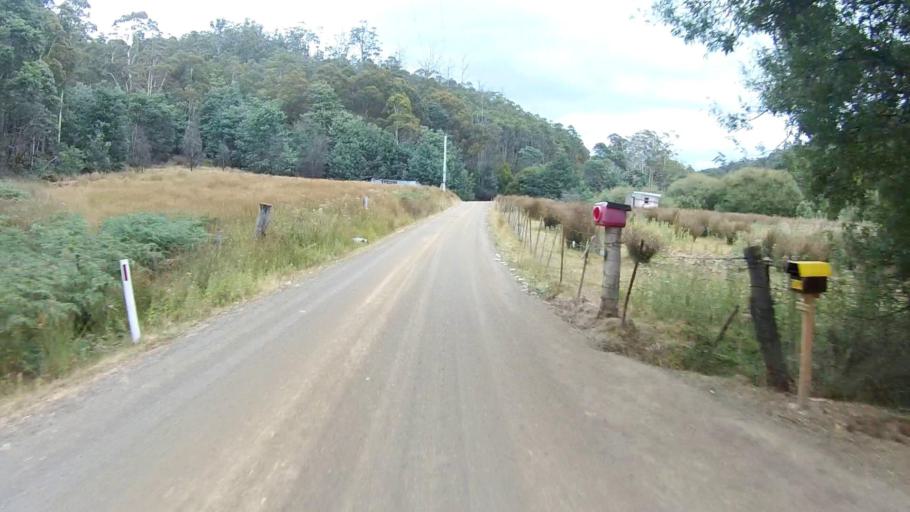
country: AU
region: Tasmania
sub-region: Huon Valley
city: Cygnet
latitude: -43.2252
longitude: 147.1698
